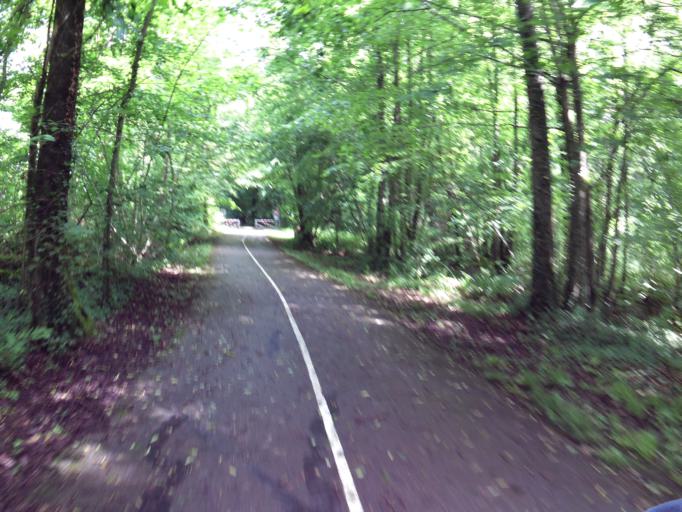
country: FR
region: Champagne-Ardenne
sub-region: Departement de l'Aube
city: Lusigny-sur-Barse
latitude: 48.2947
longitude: 4.3069
